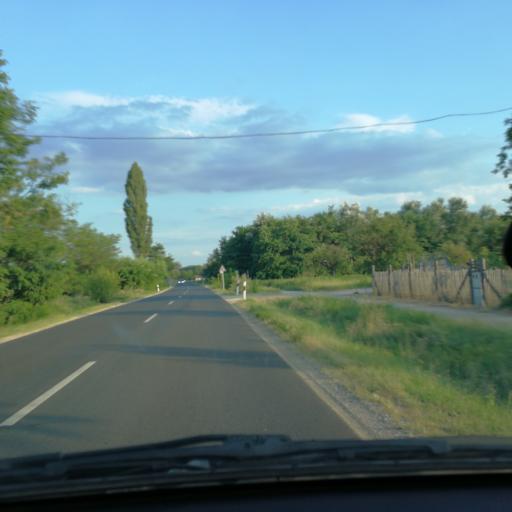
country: HU
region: Bacs-Kiskun
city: Kiskunmajsa
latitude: 46.5295
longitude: 19.7416
